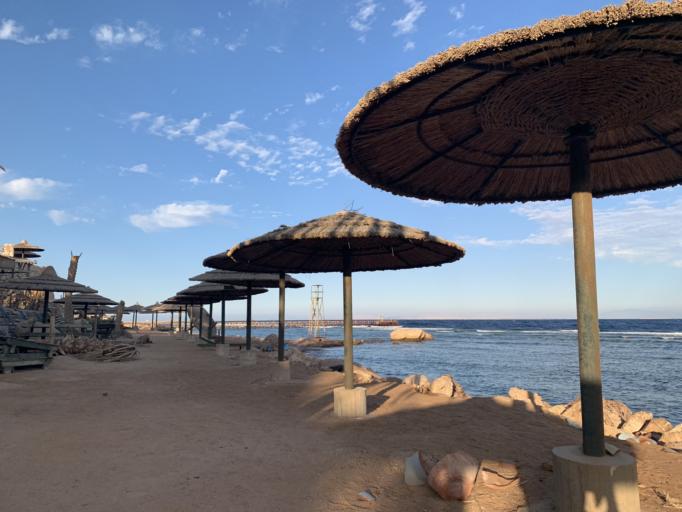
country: EG
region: South Sinai
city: Sharm el-Sheikh
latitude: 28.0148
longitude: 34.4389
